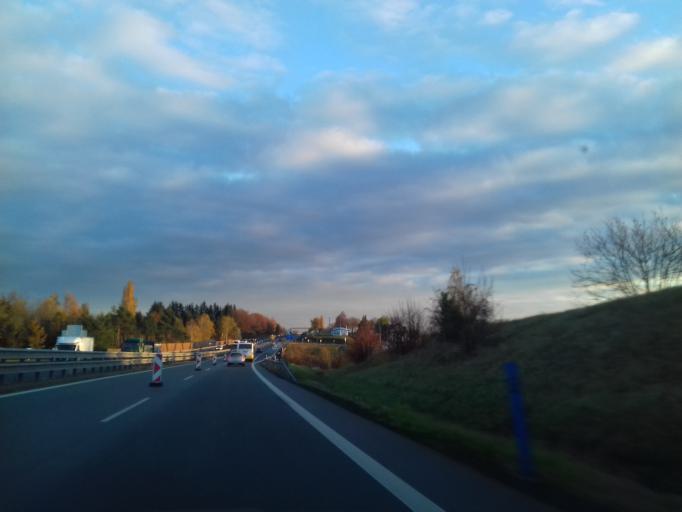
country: CZ
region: Olomoucky
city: Otaslavice
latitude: 49.4011
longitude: 17.1039
